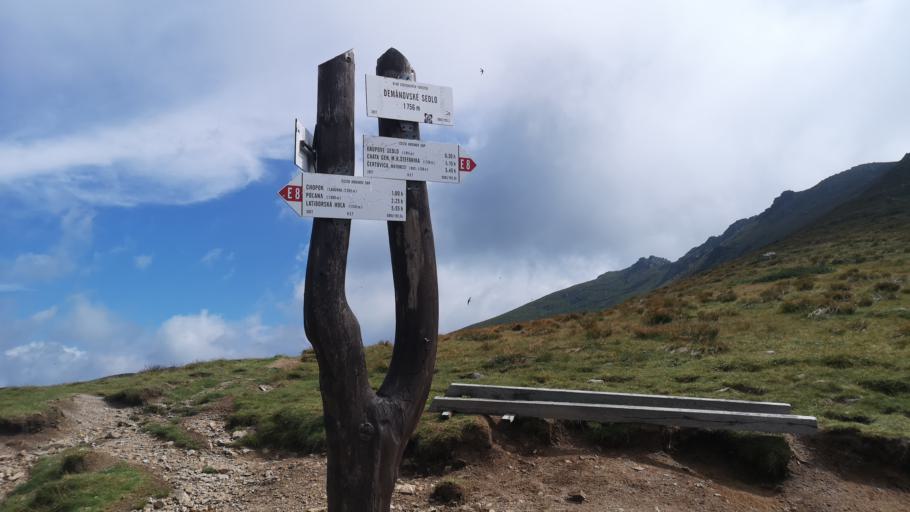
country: SK
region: Banskobystricky
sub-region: Okres Banska Bystrica
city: Brezno
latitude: 48.9393
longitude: 19.6212
